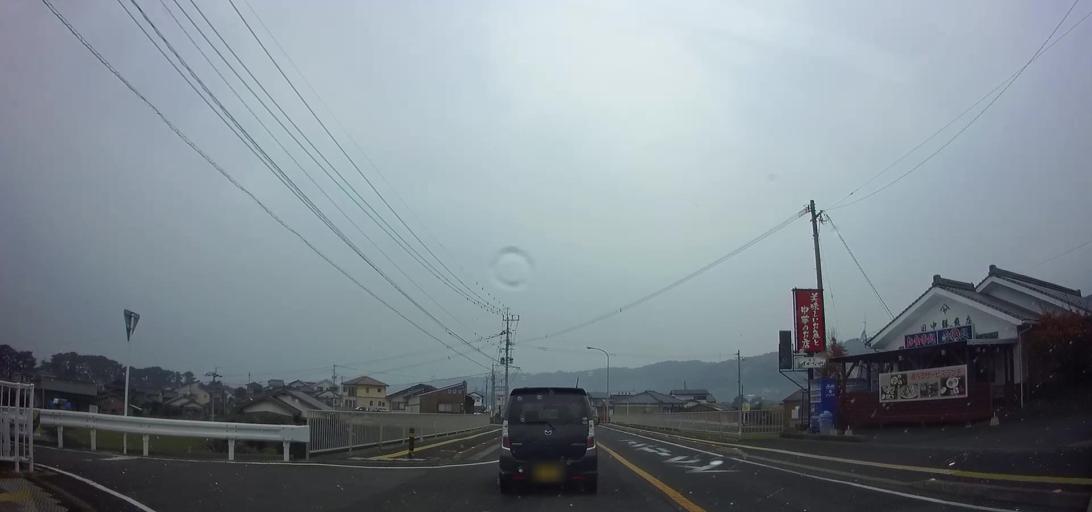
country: JP
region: Nagasaki
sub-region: Isahaya-shi
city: Isahaya
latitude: 32.7868
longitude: 130.1954
